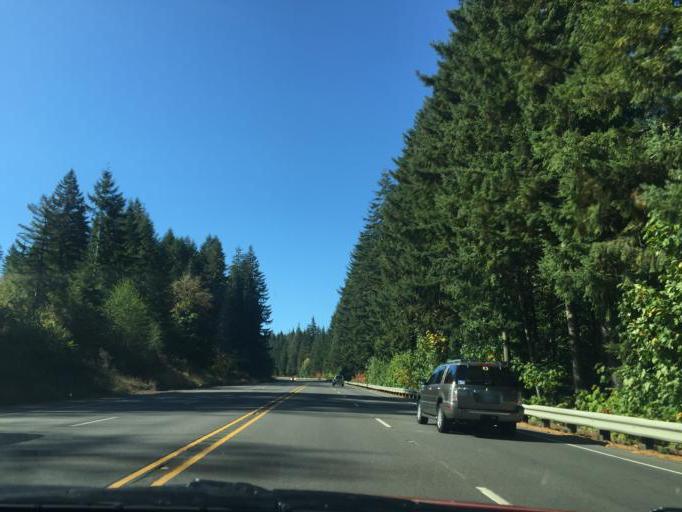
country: US
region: Oregon
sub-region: Columbia County
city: Vernonia
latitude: 45.7786
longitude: -123.3597
